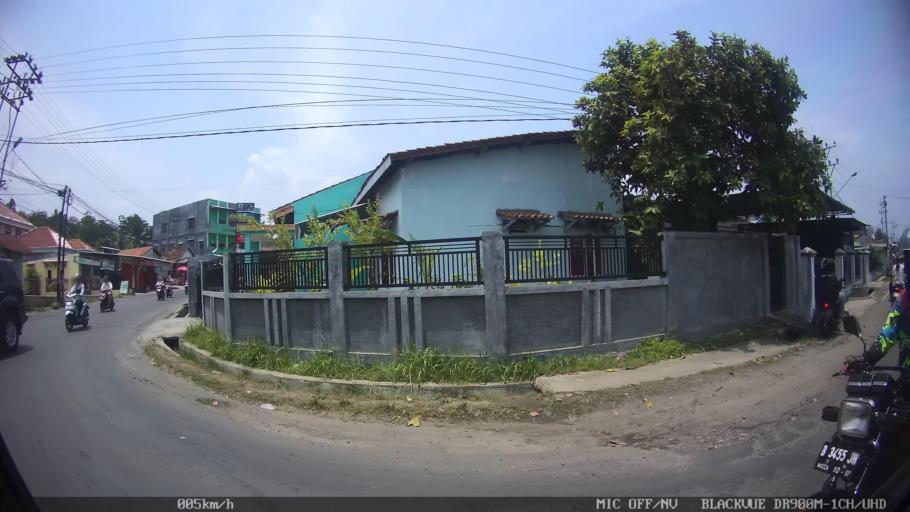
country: ID
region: Lampung
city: Bandarlampung
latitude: -5.4449
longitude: 105.2550
